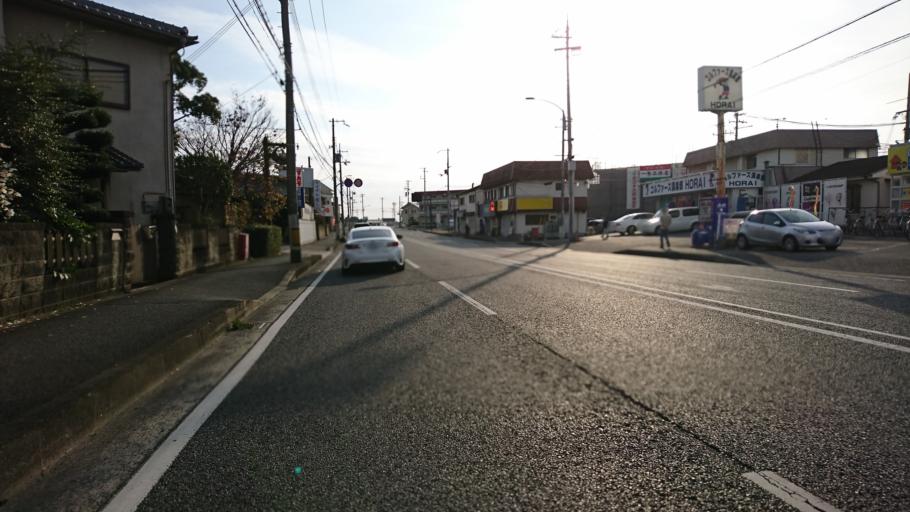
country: JP
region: Hyogo
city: Kakogawacho-honmachi
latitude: 34.7251
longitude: 134.9010
